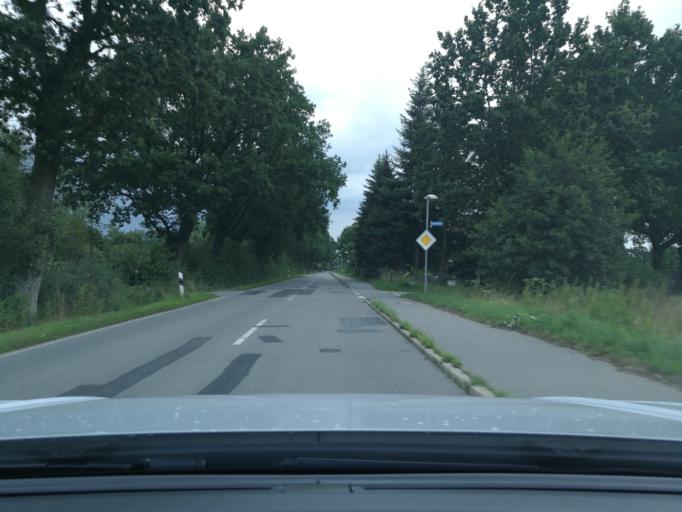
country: DE
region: Schleswig-Holstein
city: Wohltorf
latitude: 53.5414
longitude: 10.2728
